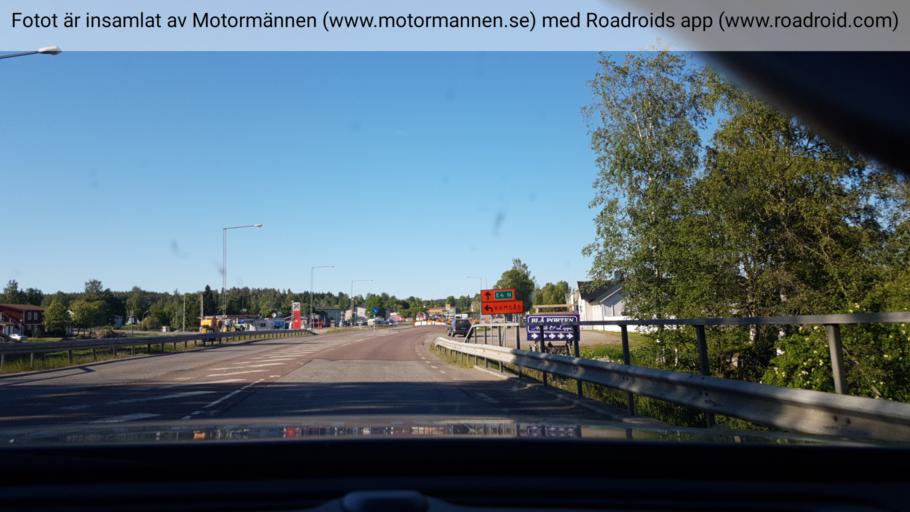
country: SE
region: Vaesternorrland
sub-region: Haernoesands Kommun
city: Haernoesand
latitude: 62.6723
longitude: 17.8398
